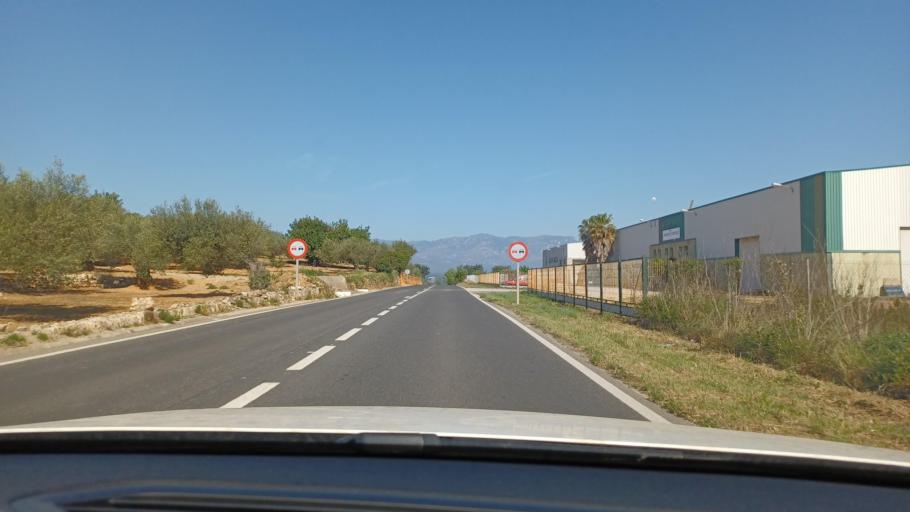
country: ES
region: Catalonia
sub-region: Provincia de Tarragona
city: Masdenverge
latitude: 40.7095
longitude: 0.5399
